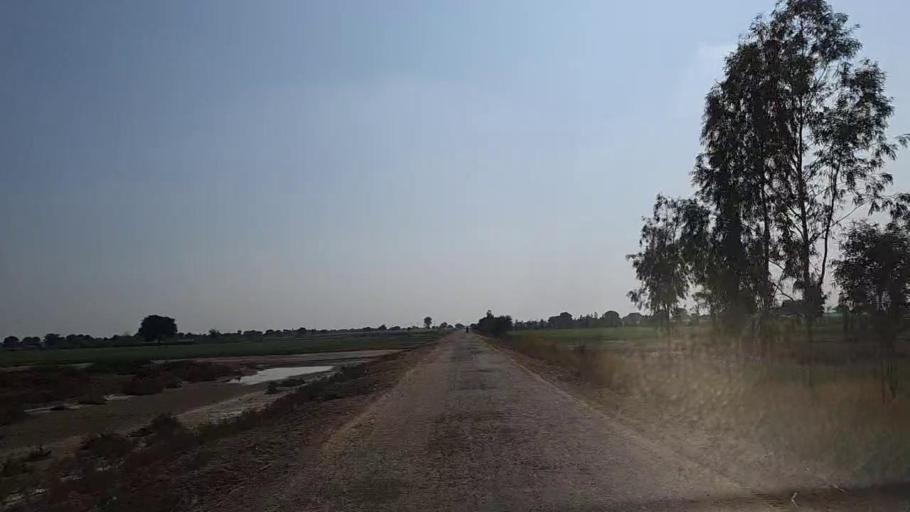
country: PK
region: Sindh
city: Jam Sahib
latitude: 26.2675
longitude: 68.5672
